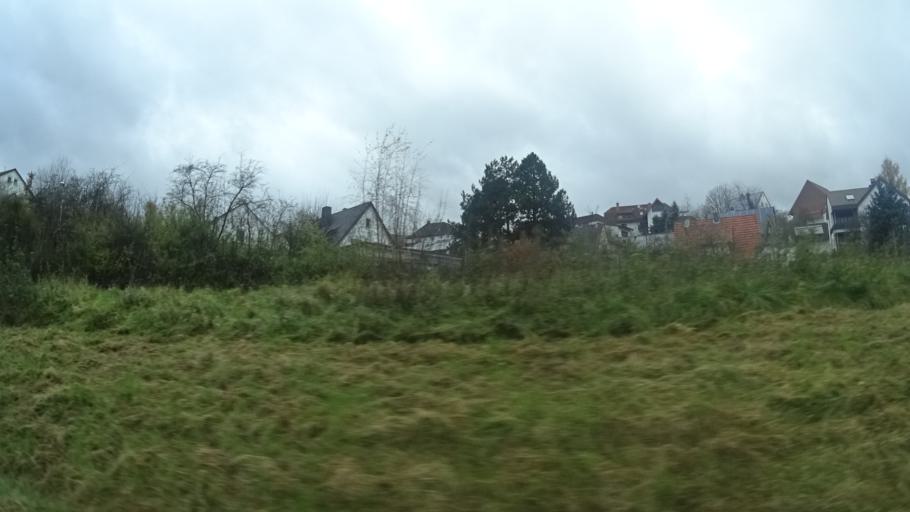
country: DE
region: Hesse
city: Heringen
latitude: 50.9052
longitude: 10.0129
